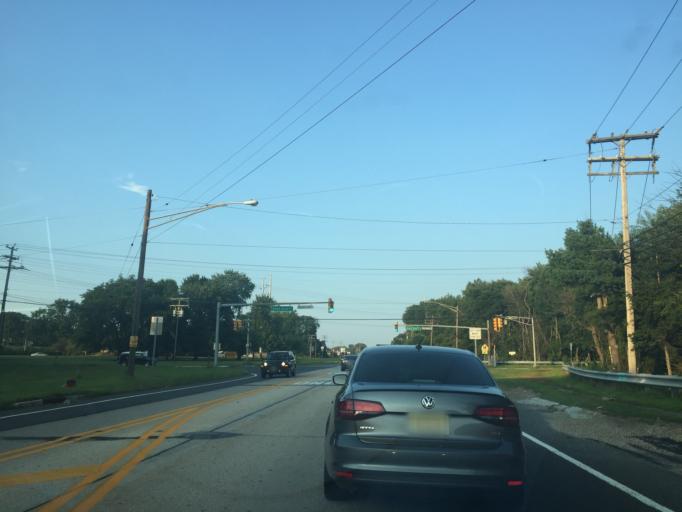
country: US
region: New Jersey
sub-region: Monmouth County
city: Shark River Hills
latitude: 40.2263
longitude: -74.0743
